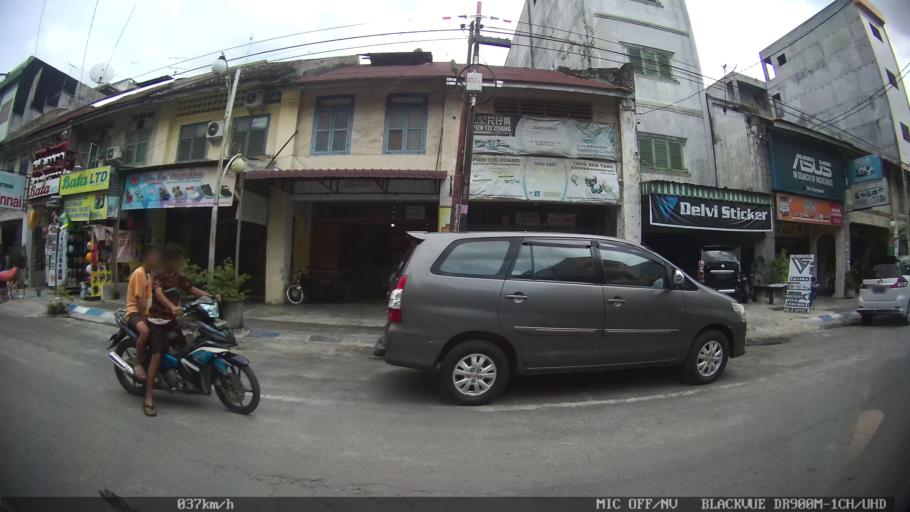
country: ID
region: North Sumatra
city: Percut
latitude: 3.5618
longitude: 98.8763
